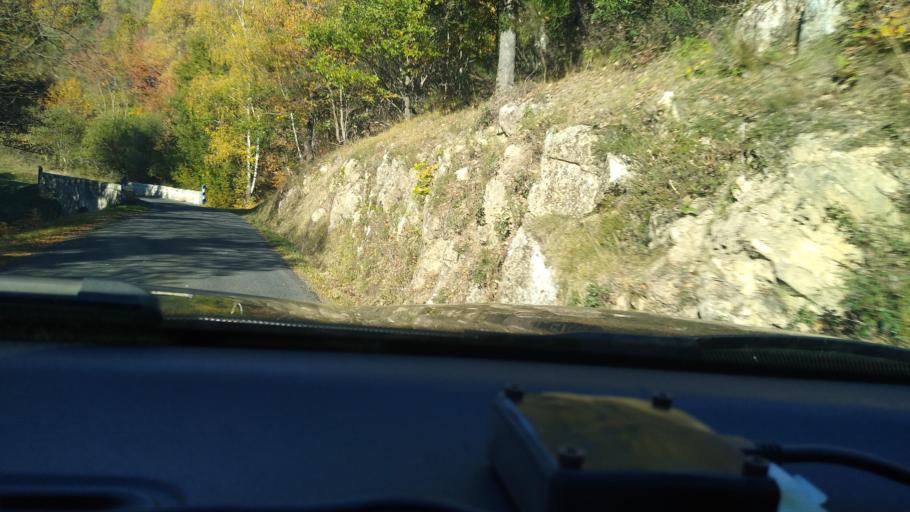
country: FR
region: Languedoc-Roussillon
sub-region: Departement de l'Aude
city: Quillan
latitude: 42.7244
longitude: 2.1218
